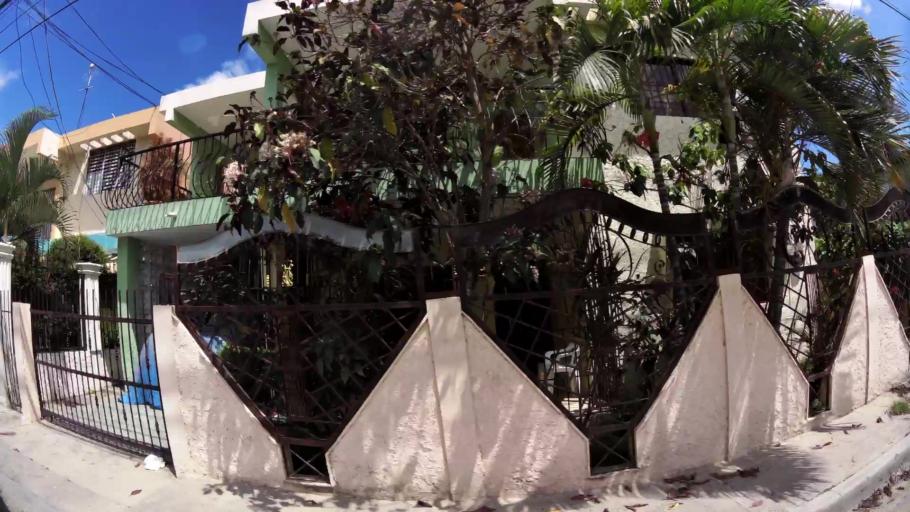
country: DO
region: San Cristobal
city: San Cristobal
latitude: 18.4183
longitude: -70.0974
